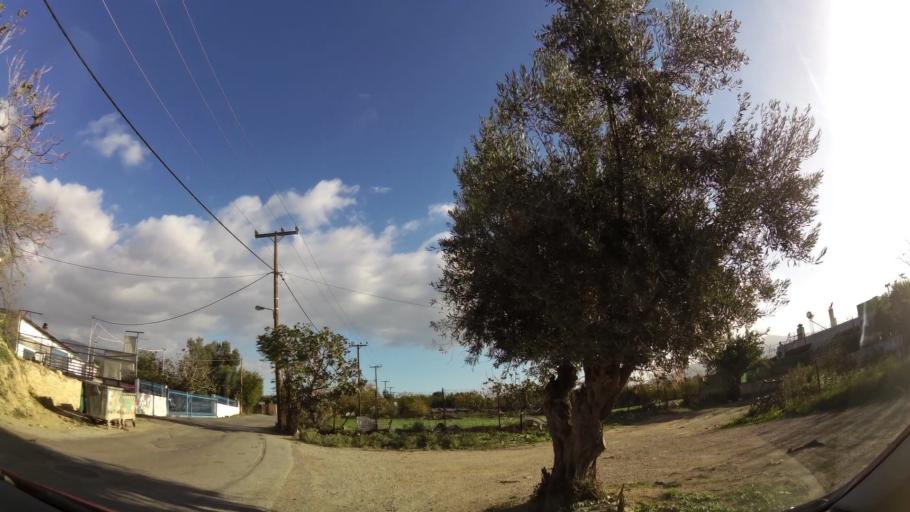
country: GR
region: Attica
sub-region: Nomarchia Athinas
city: Metamorfosi
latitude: 38.0684
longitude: 23.7485
